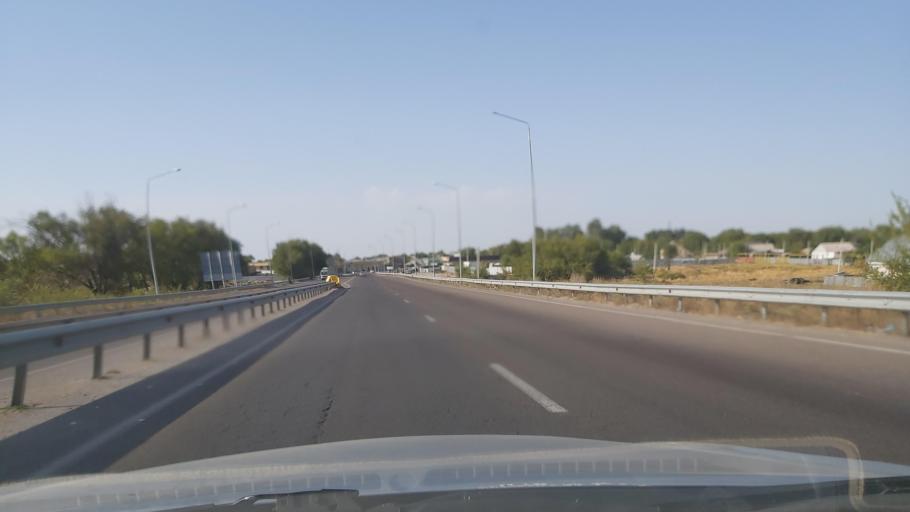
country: KZ
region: Almaty Oblysy
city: Energeticheskiy
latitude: 43.4729
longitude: 77.0317
